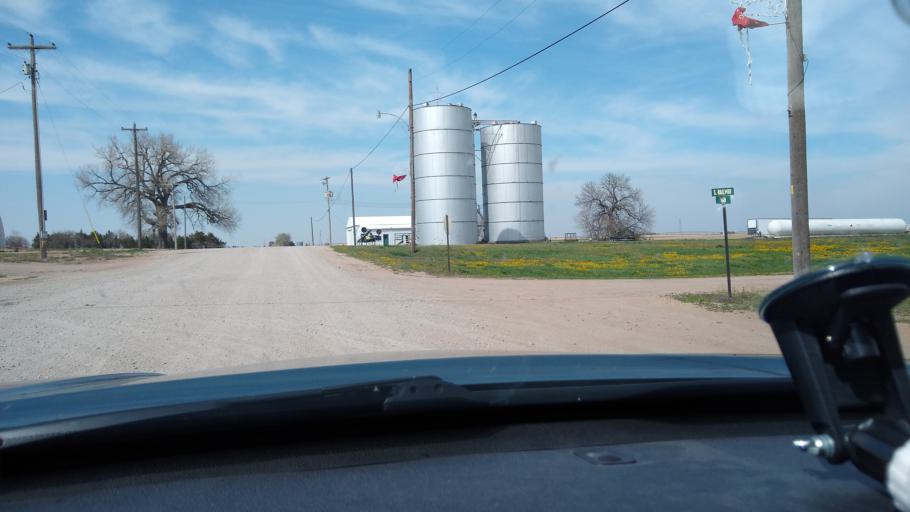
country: US
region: Nebraska
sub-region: Fillmore County
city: Geneva
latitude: 40.4154
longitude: -97.5868
